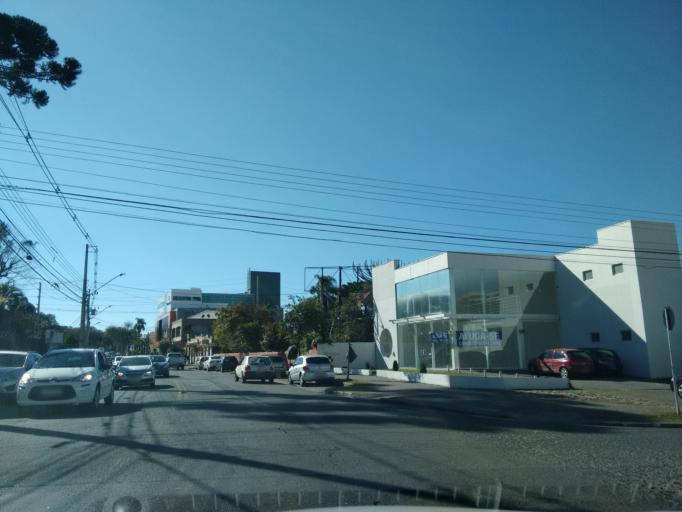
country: BR
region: Parana
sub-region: Curitiba
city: Curitiba
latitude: -25.4060
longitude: -49.2711
